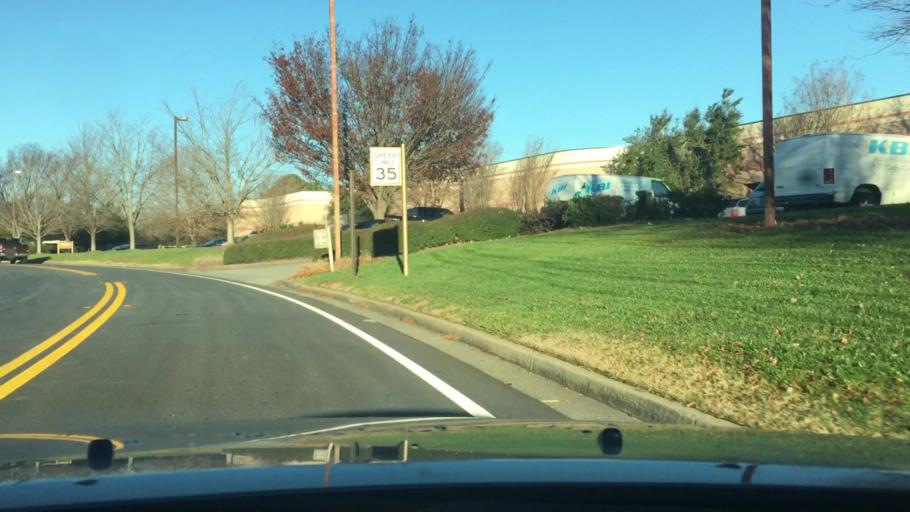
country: US
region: Georgia
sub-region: Cobb County
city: Kennesaw
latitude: 34.0042
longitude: -84.5965
